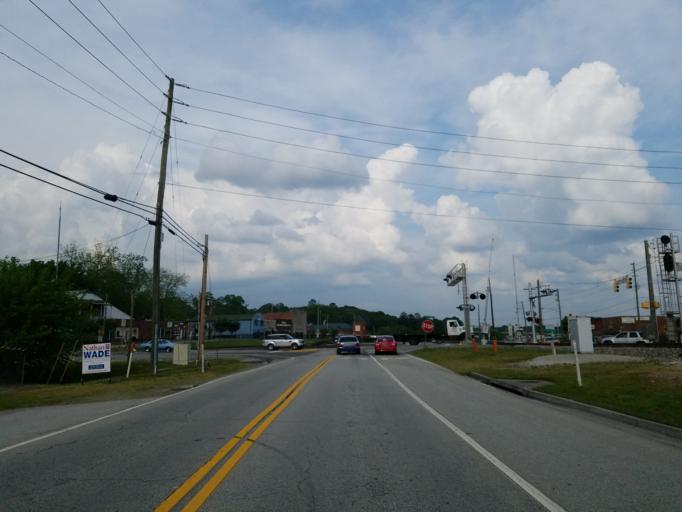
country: US
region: Georgia
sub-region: Cobb County
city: Austell
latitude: 33.8130
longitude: -84.6353
